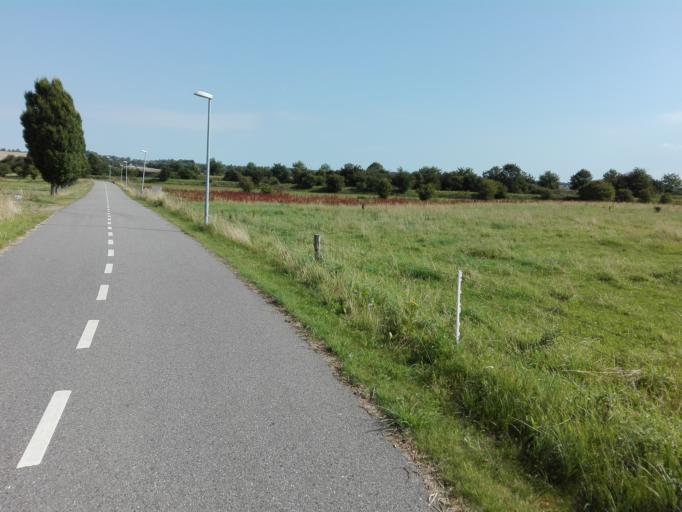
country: DK
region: Central Jutland
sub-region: Arhus Kommune
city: Lystrup
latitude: 56.2133
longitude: 10.2080
